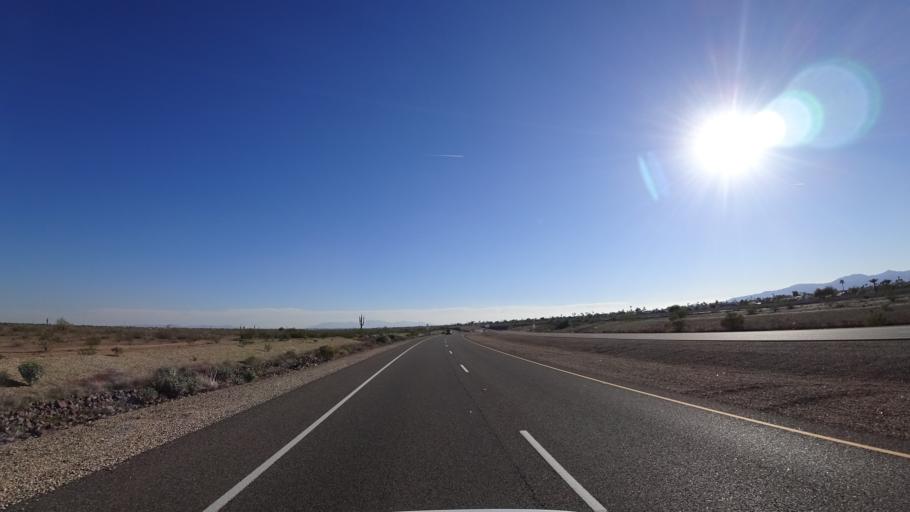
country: US
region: Arizona
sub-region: Maricopa County
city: Sun City West
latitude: 33.6685
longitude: -112.3228
